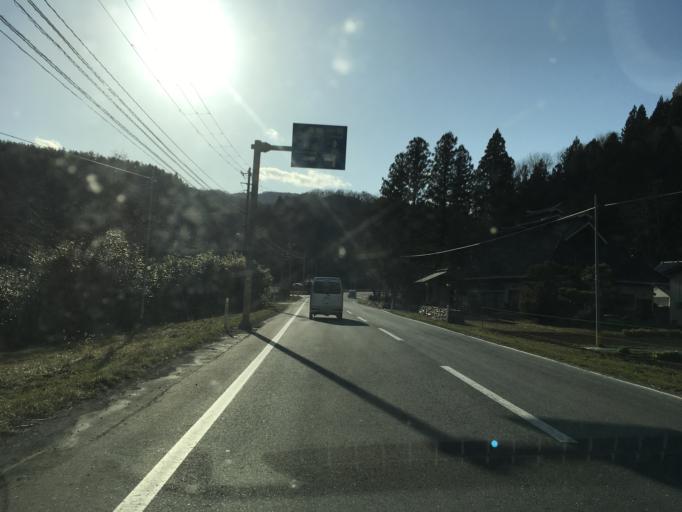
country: JP
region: Iwate
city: Ofunato
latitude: 39.0214
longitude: 141.5502
